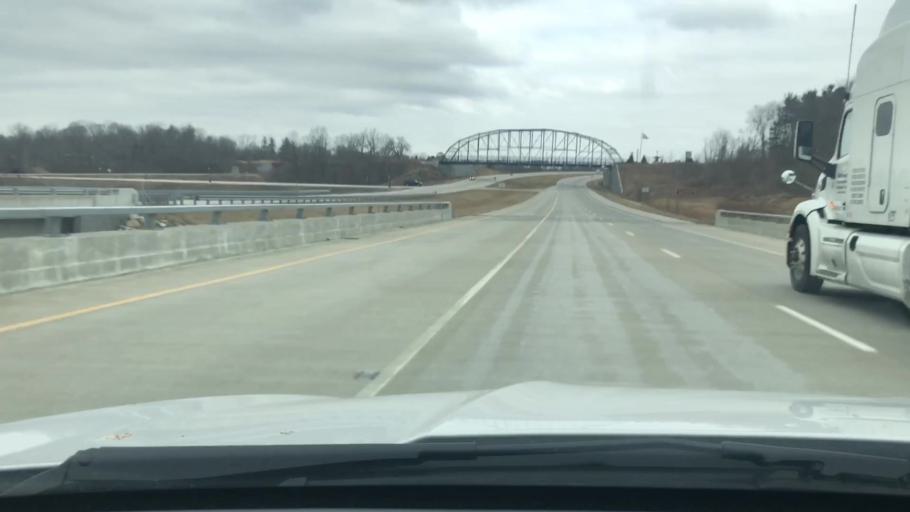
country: US
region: Indiana
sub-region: Carroll County
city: Delphi
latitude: 40.5915
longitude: -86.6533
